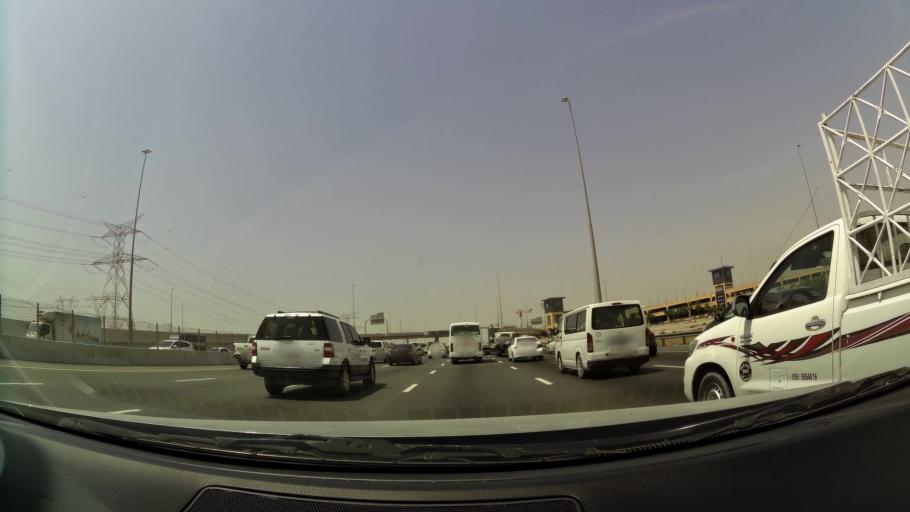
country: AE
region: Ash Shariqah
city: Sharjah
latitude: 25.2145
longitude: 55.4024
